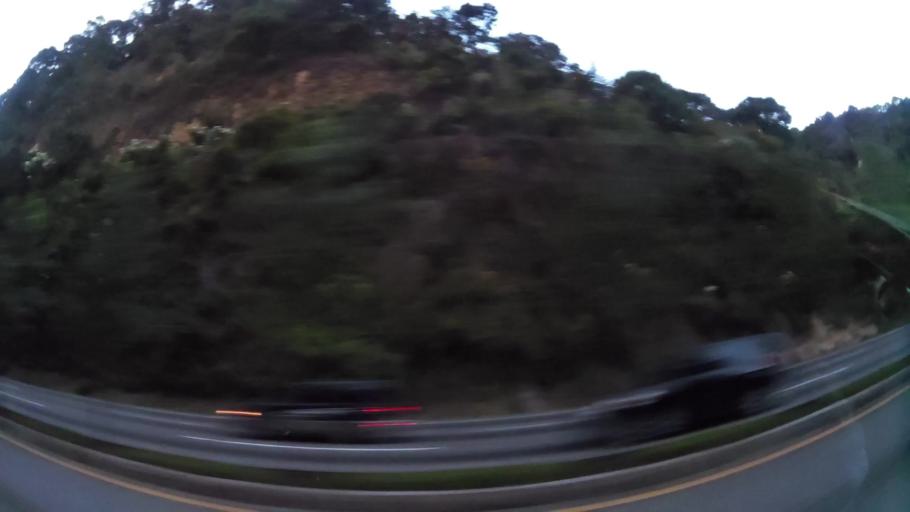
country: GT
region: Sacatepequez
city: San Lucas Sacatepequez
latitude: 14.6072
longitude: -90.6336
